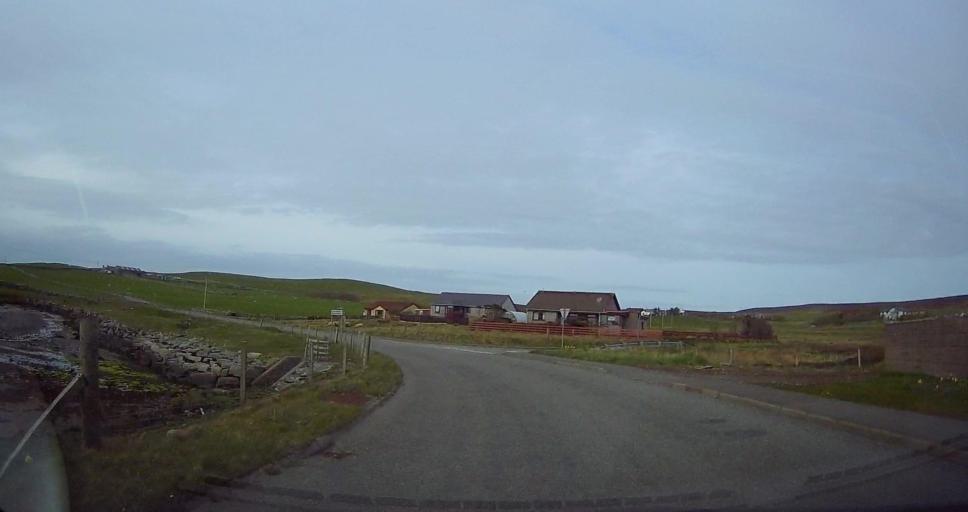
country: GB
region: Scotland
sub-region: Shetland Islands
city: Shetland
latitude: 60.1572
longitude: -1.1154
